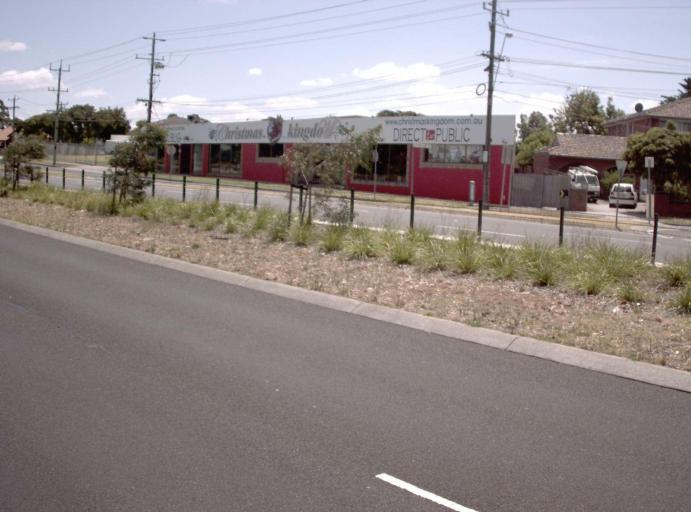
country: AU
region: Victoria
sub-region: Kingston
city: Parkdale
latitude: -37.9878
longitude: 145.0794
